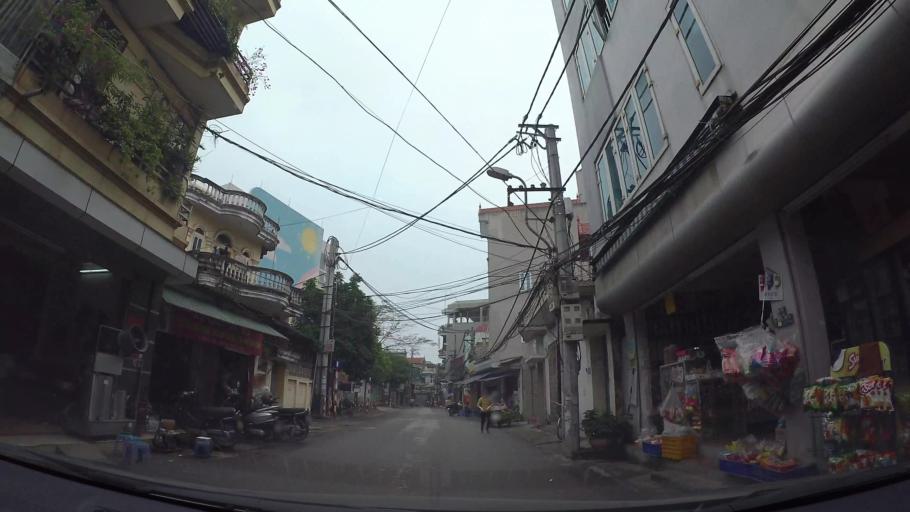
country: VN
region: Ha Noi
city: Van Dien
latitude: 20.9662
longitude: 105.8733
